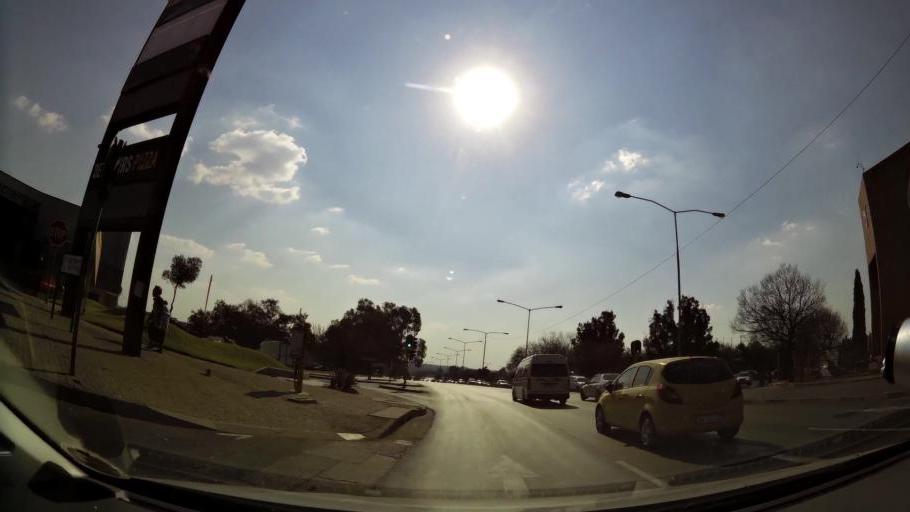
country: ZA
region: Gauteng
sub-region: City of Johannesburg Metropolitan Municipality
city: Modderfontein
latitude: -26.1023
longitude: 28.2263
